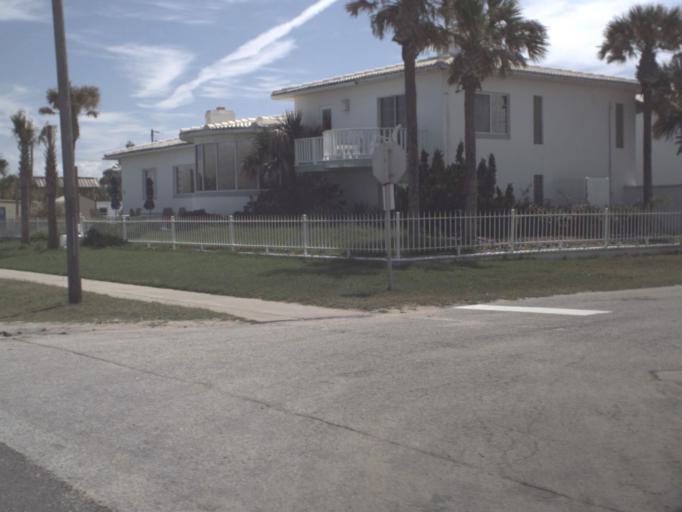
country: US
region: Florida
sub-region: Flagler County
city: Flagler Beach
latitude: 29.4747
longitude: -81.1244
